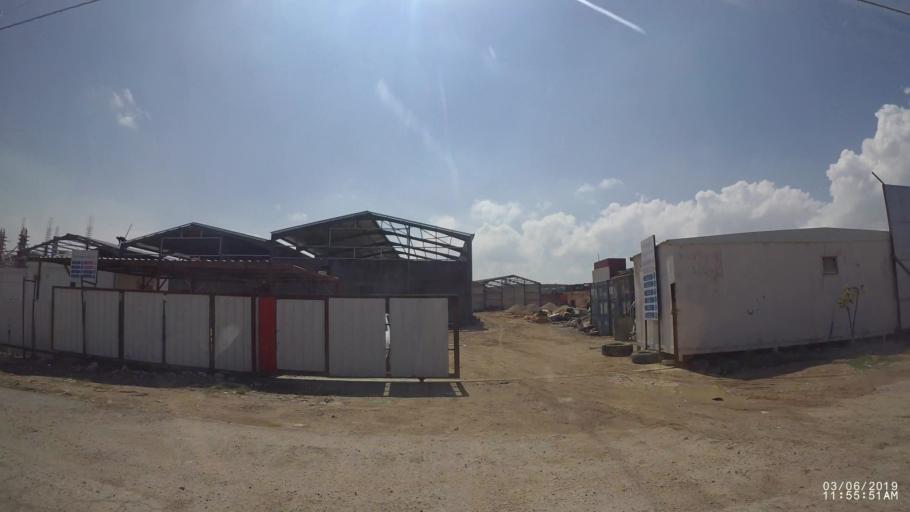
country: JO
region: Zarqa
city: Russeifa
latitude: 31.9841
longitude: 36.0118
